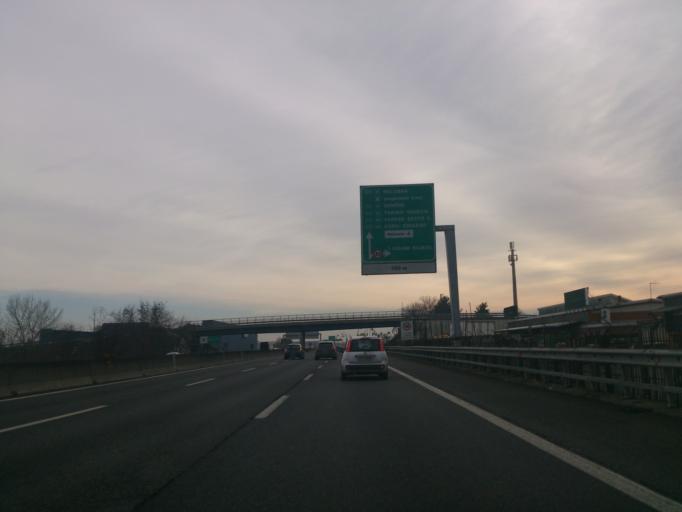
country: IT
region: Lombardy
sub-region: Citta metropolitana di Milano
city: Civesio
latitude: 45.3996
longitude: 9.2606
